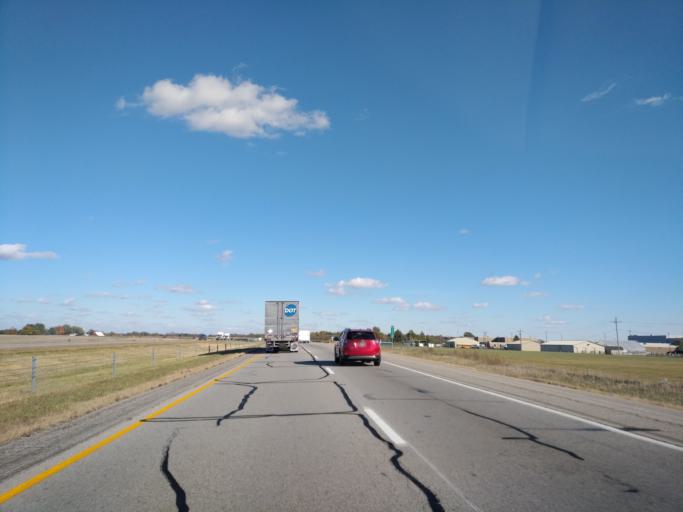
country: US
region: Indiana
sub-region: Henry County
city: Knightstown
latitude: 39.8259
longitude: -85.6145
